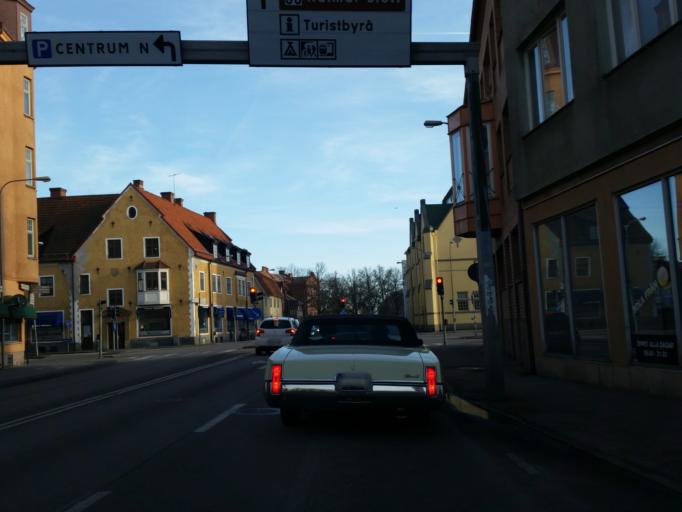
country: SE
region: Kalmar
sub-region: Kalmar Kommun
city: Kalmar
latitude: 56.6659
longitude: 16.3543
